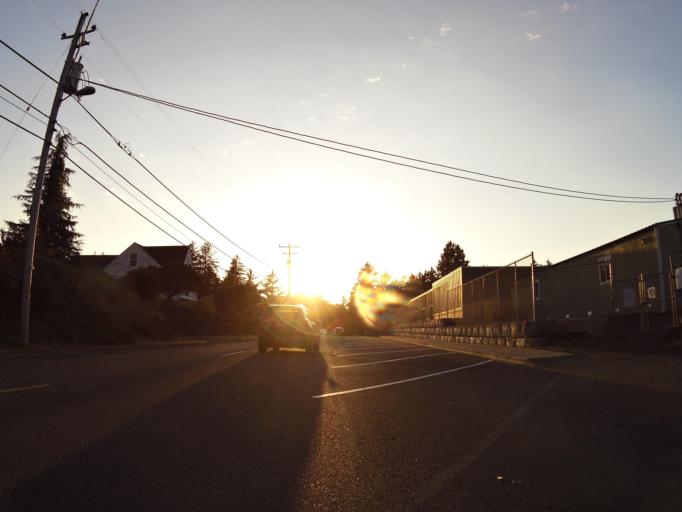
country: US
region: Oregon
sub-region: Clatsop County
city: Warrenton
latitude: 46.1577
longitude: -123.9309
